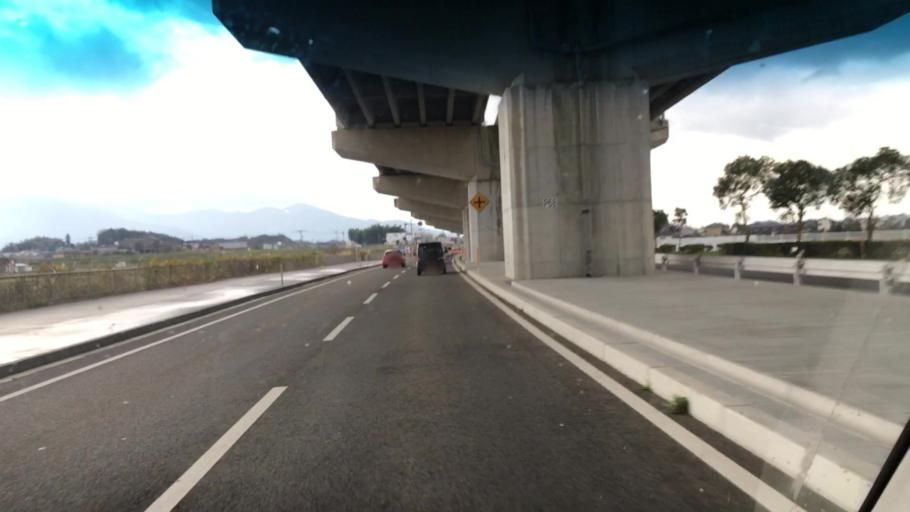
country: JP
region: Fukuoka
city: Maebaru-chuo
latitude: 33.5522
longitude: 130.2215
